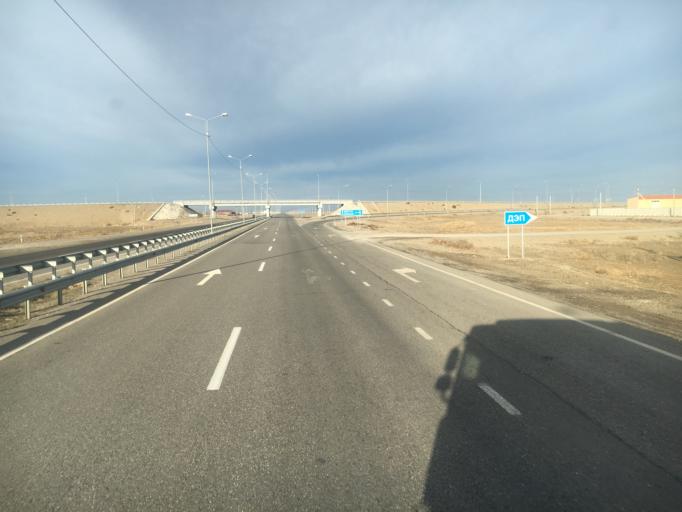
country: KZ
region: Ongtustik Qazaqstan
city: Turkestan
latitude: 43.4134
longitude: 68.0282
